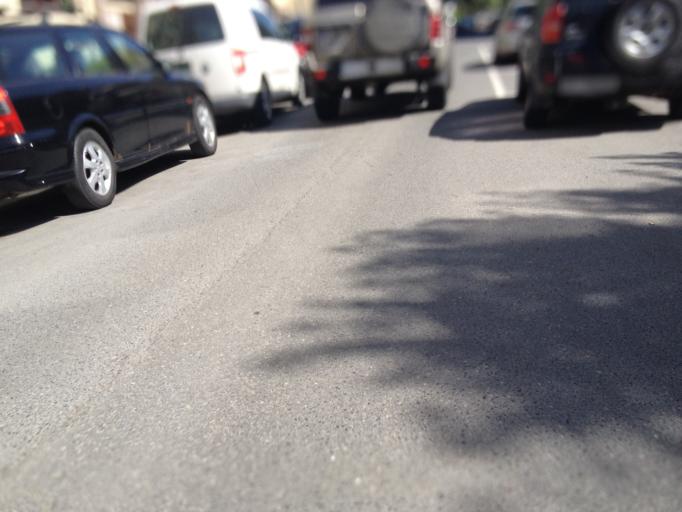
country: NO
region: Oslo
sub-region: Oslo
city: Oslo
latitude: 59.9364
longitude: 10.7638
